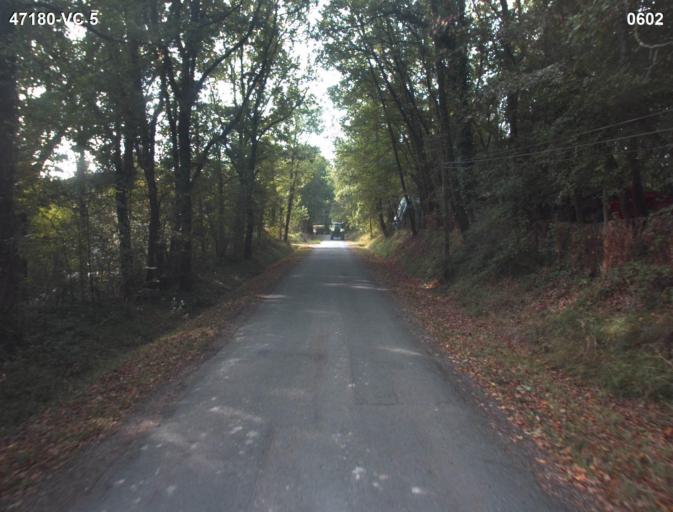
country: FR
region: Aquitaine
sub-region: Departement du Lot-et-Garonne
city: Sainte-Colombe-en-Bruilhois
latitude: 44.1775
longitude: 0.4679
